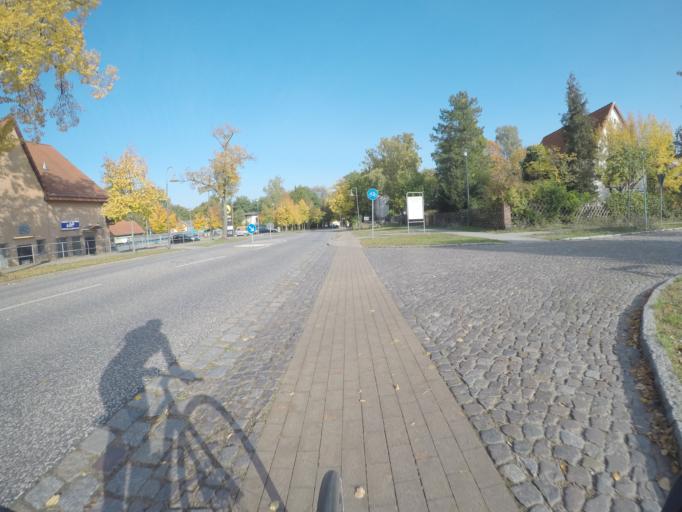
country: DE
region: Brandenburg
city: Birkenwerder
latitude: 52.6860
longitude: 13.2827
